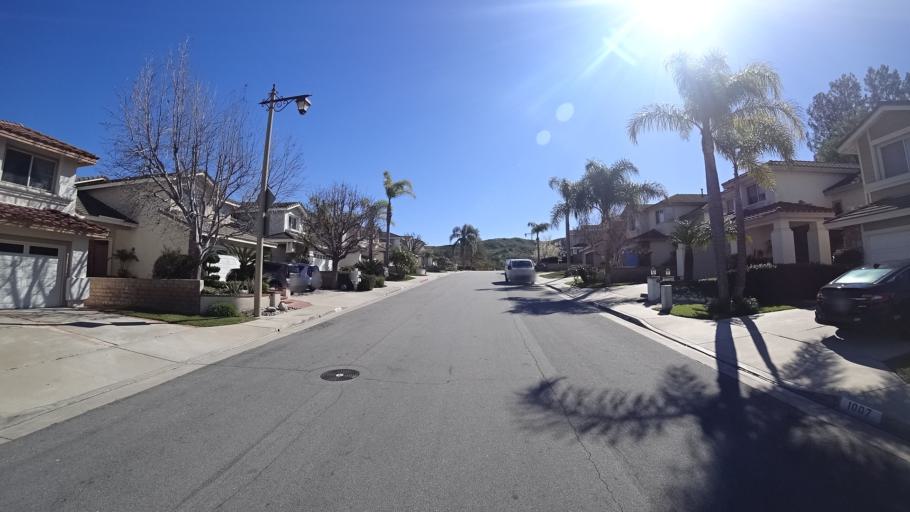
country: US
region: California
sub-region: Orange County
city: Yorba Linda
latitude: 33.8546
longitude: -117.7299
